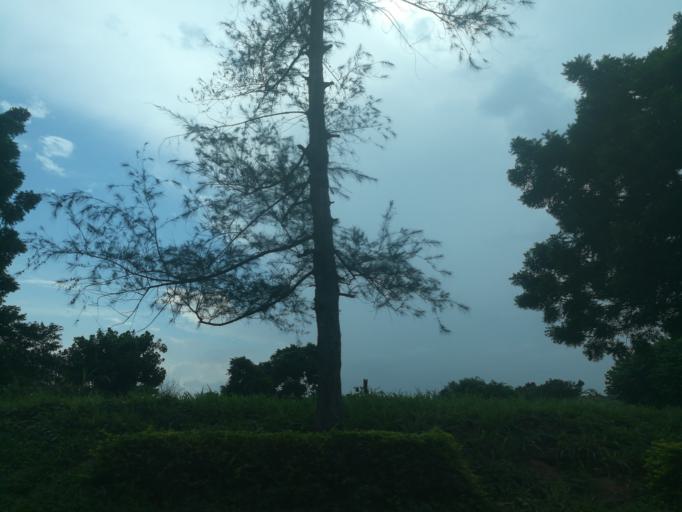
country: NG
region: Lagos
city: Ikorodu
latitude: 6.6393
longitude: 3.5211
